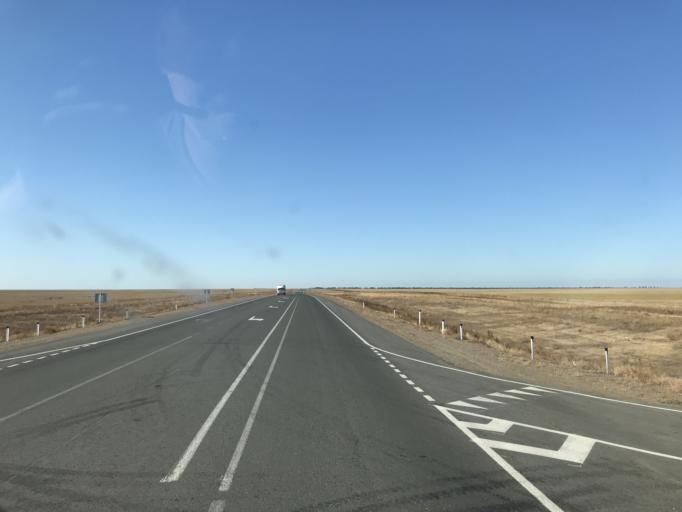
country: KZ
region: Pavlodar
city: Kurchatov
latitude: 51.1501
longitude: 78.7760
